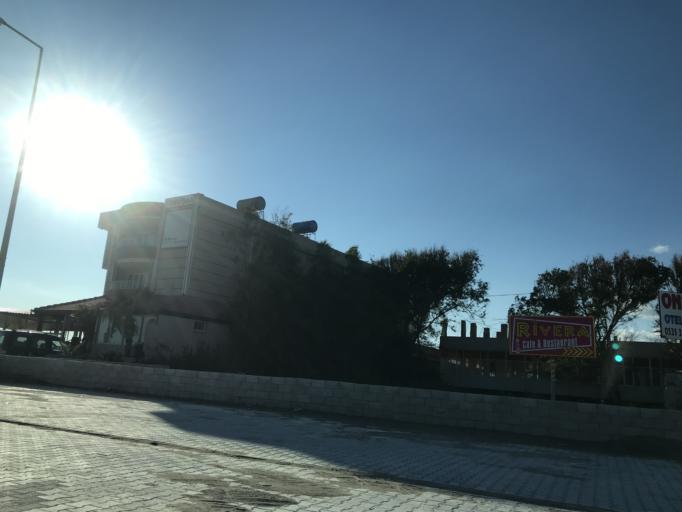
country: TR
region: Hatay
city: Samandag
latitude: 36.0821
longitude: 35.9458
